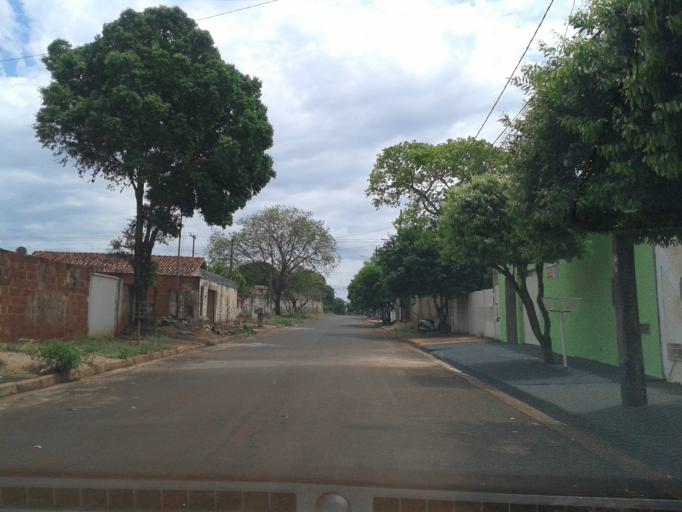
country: BR
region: Minas Gerais
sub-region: Ituiutaba
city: Ituiutaba
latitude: -18.9957
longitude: -49.4611
